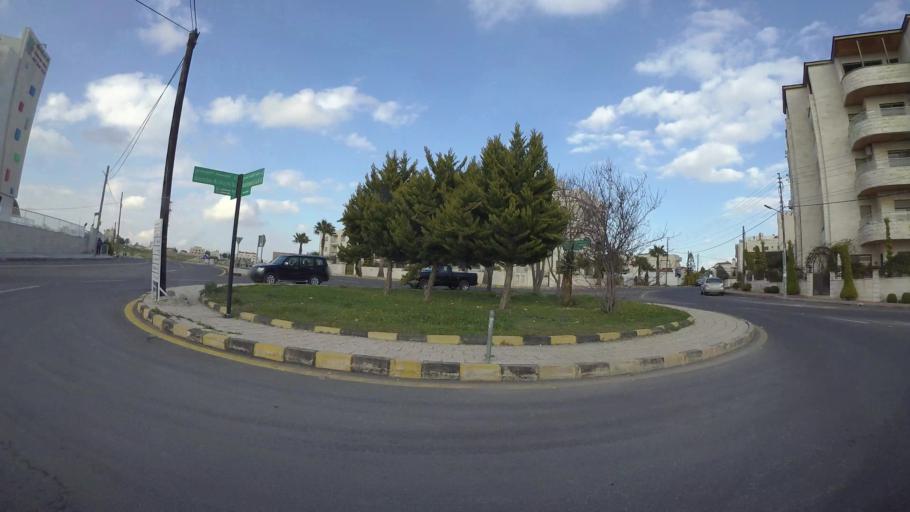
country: JO
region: Amman
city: Umm as Summaq
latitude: 31.9074
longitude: 35.8699
